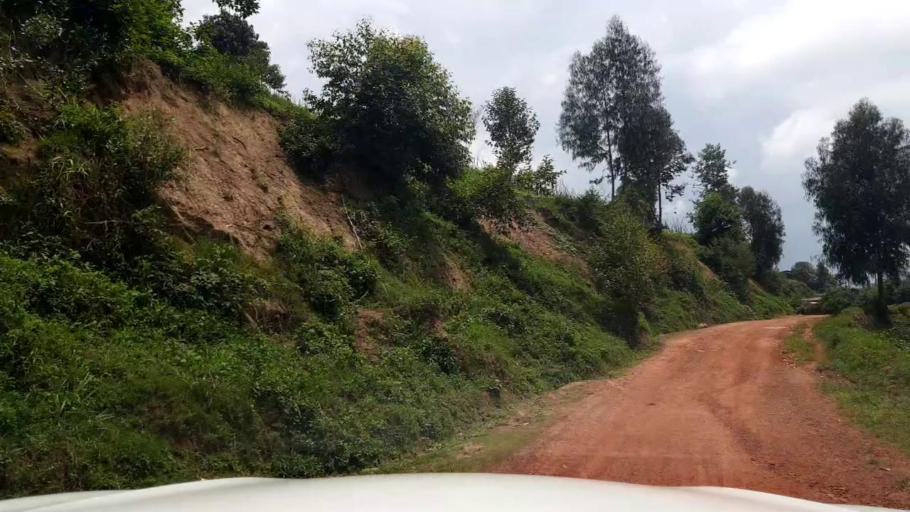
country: RW
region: Northern Province
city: Byumba
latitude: -1.4843
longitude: 29.9240
